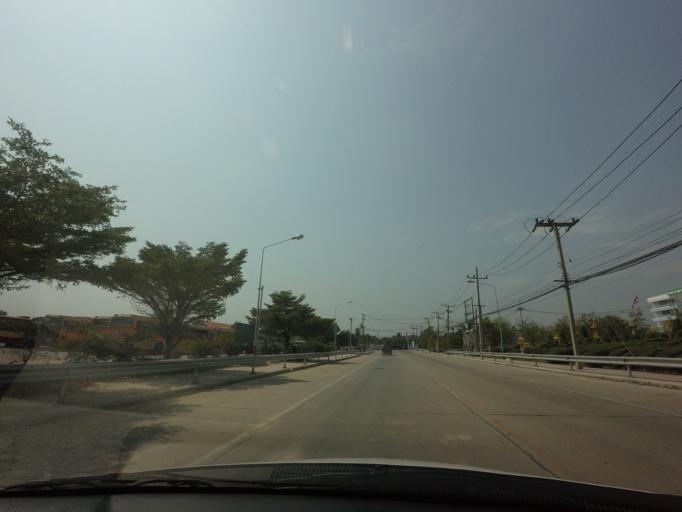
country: TH
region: Nakhon Pathom
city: Sam Phran
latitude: 13.7462
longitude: 100.2618
